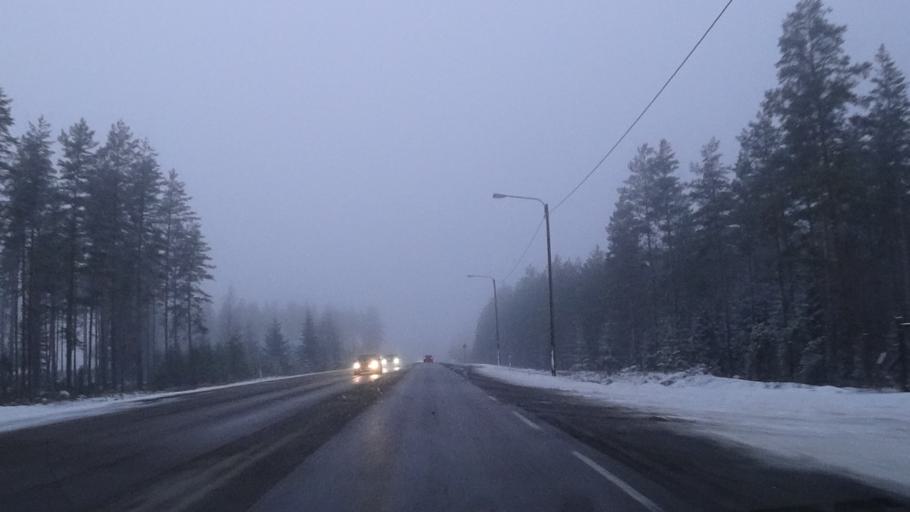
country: FI
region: Paijanne Tavastia
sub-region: Lahti
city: Hollola
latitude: 60.9894
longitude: 25.3889
